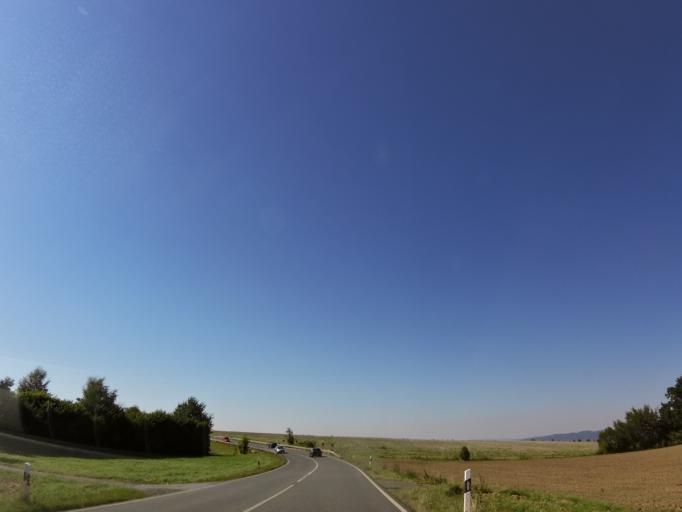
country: DE
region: Saxony
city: Struppen
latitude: 50.9211
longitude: 14.0108
